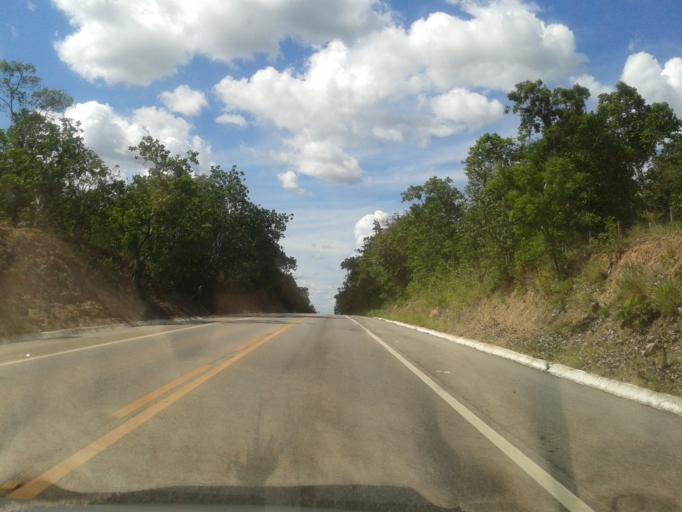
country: BR
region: Goias
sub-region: Itapuranga
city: Itapuranga
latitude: -15.5387
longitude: -50.2907
